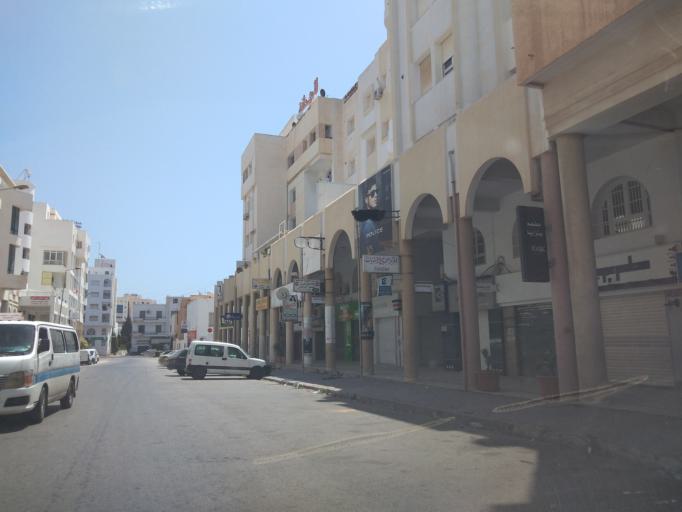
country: TN
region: Safaqis
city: Sfax
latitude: 34.7366
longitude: 10.7527
